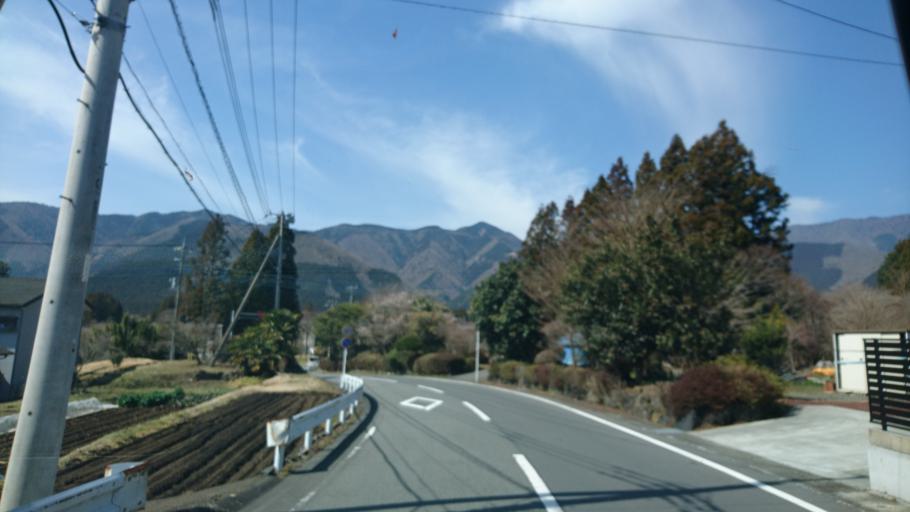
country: JP
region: Shizuoka
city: Fujinomiya
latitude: 35.3587
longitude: 138.5712
